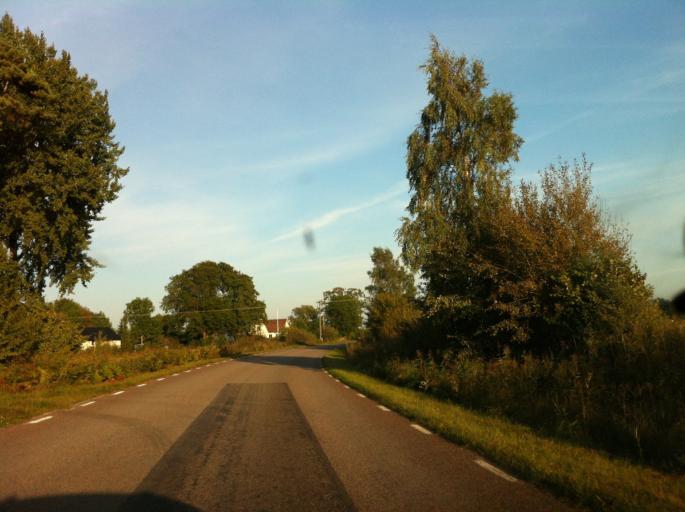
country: SE
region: Gotland
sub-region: Gotland
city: Slite
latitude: 57.4198
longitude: 18.8666
